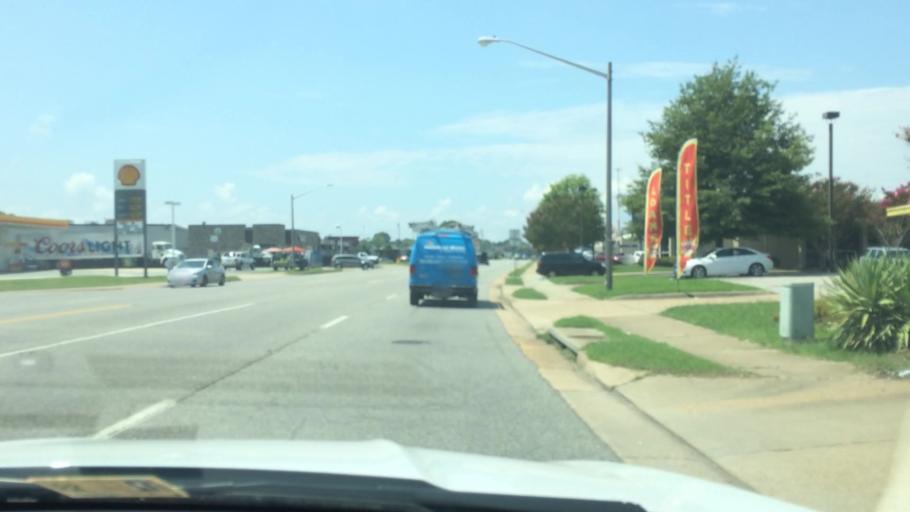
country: US
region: Virginia
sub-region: York County
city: Yorktown
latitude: 37.1311
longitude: -76.5332
